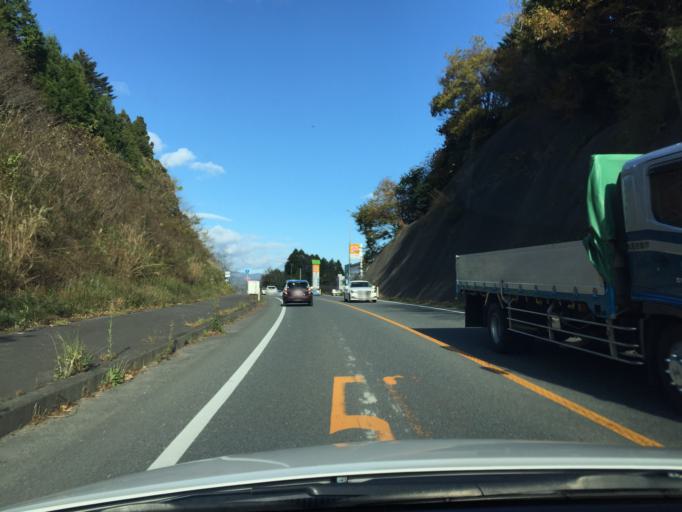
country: JP
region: Fukushima
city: Iwaki
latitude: 37.1943
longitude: 140.9992
